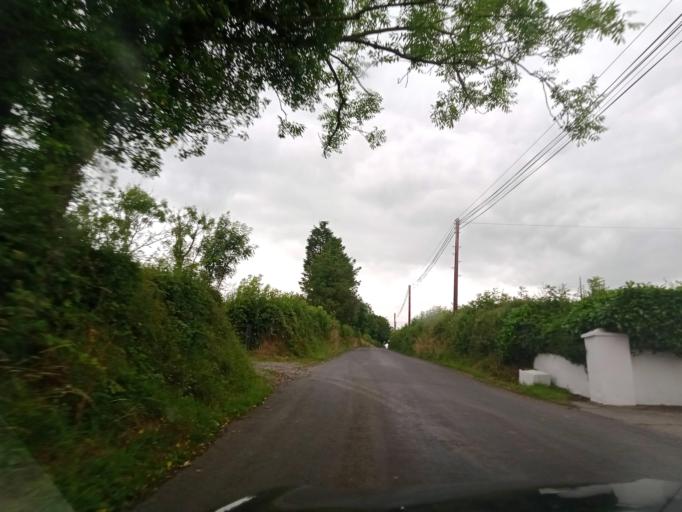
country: IE
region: Leinster
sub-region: Kilkenny
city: Castlecomer
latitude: 52.8911
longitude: -7.1567
